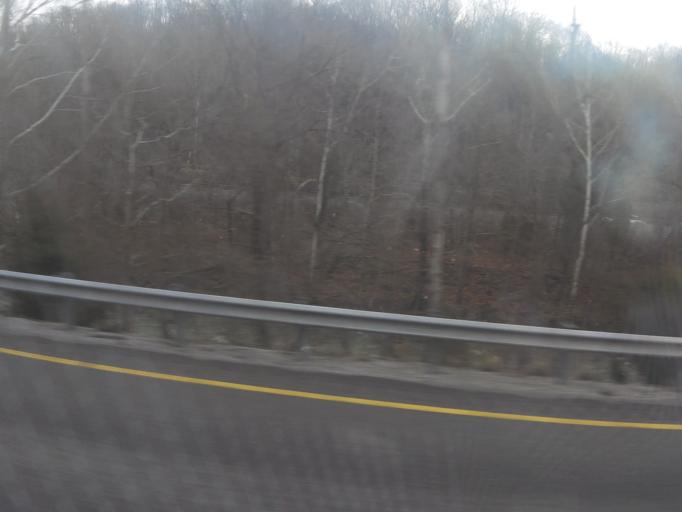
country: US
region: Tennessee
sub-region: Marion County
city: Jasper
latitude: 35.0071
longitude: -85.5272
